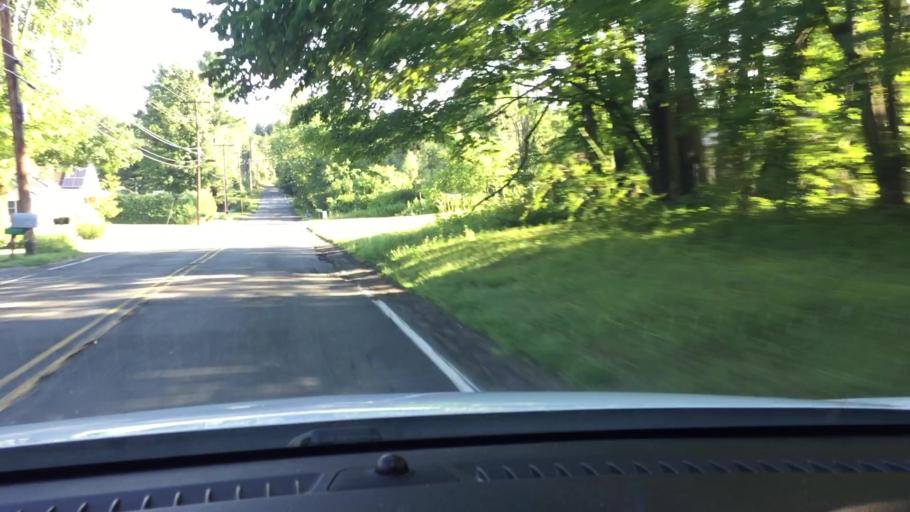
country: US
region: Massachusetts
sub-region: Berkshire County
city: Pittsfield
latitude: 42.4287
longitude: -73.2259
